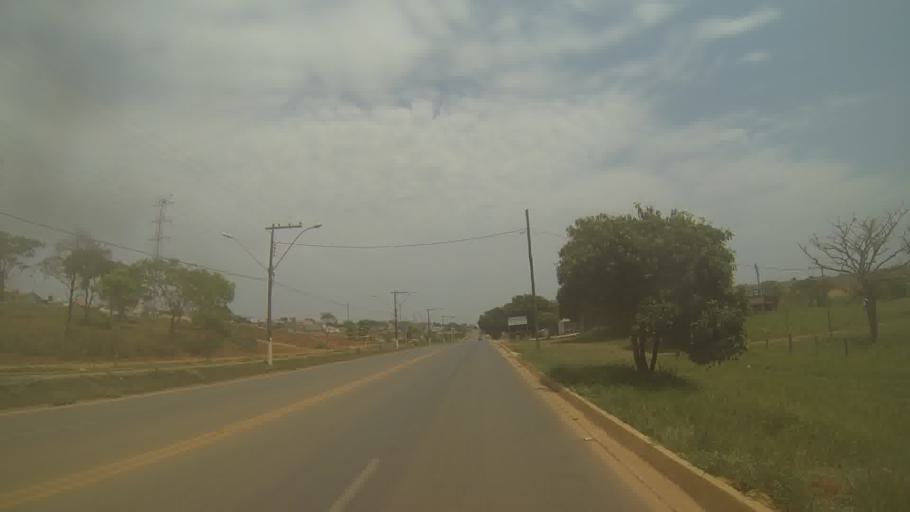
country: BR
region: Minas Gerais
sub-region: Bambui
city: Bambui
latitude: -20.0153
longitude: -45.9607
